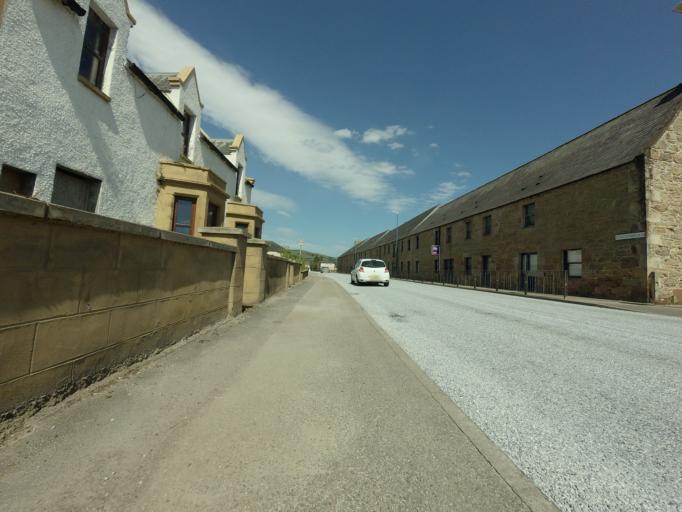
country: GB
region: Scotland
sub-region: Highland
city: Dingwall
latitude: 57.5899
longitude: -4.4242
